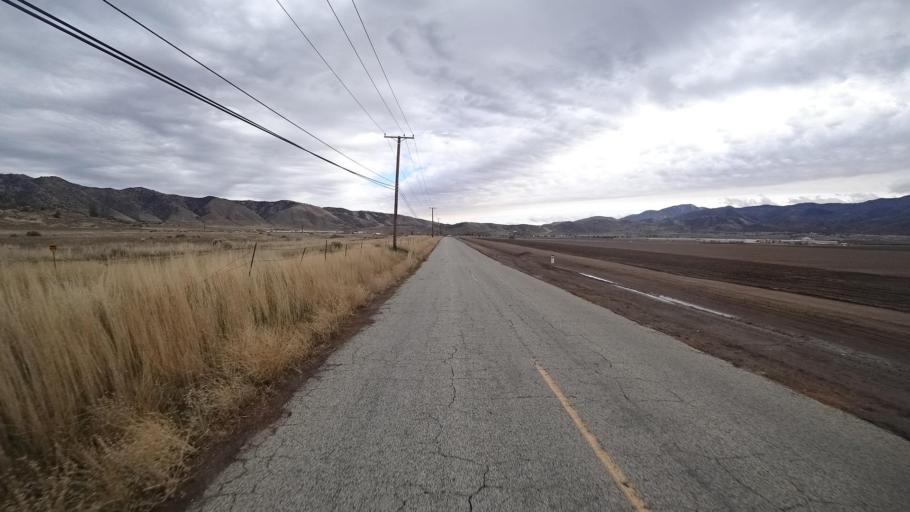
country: US
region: California
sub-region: Kern County
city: Bear Valley Springs
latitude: 35.1235
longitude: -118.6079
